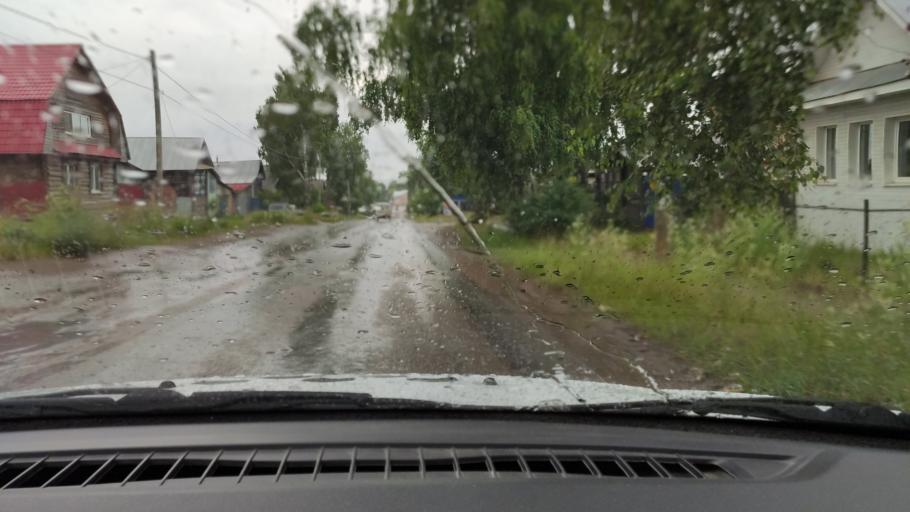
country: RU
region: Udmurtiya
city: Votkinsk
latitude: 57.0655
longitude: 54.0059
